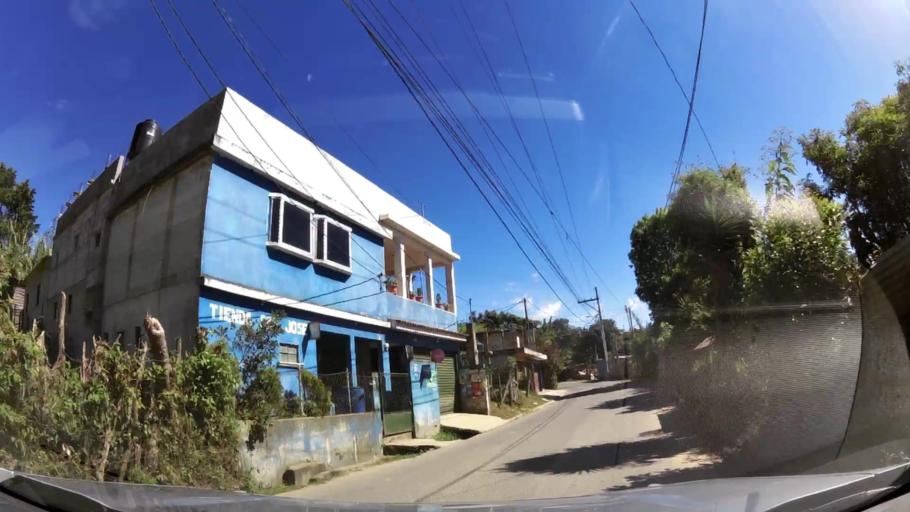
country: GT
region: Guatemala
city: San Jose Pinula
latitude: 14.5255
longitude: -90.4163
